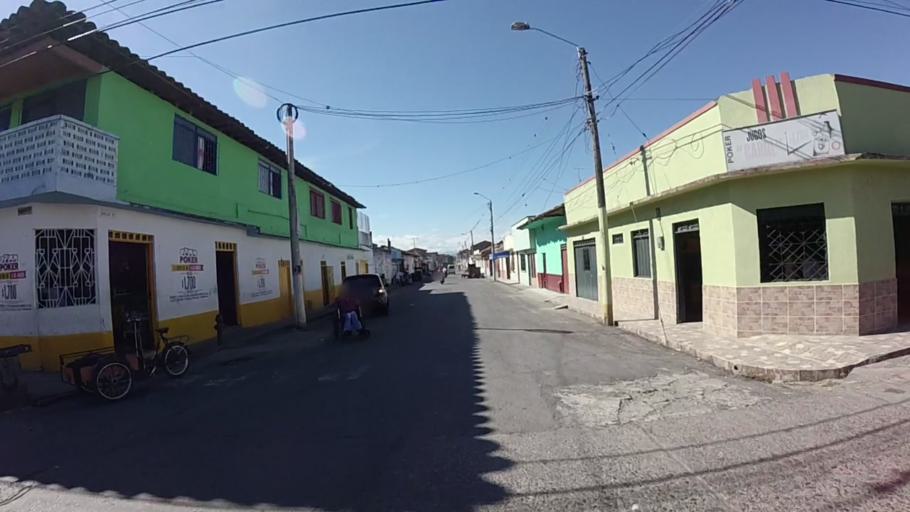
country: CO
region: Valle del Cauca
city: Cartago
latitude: 4.7476
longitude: -75.9064
